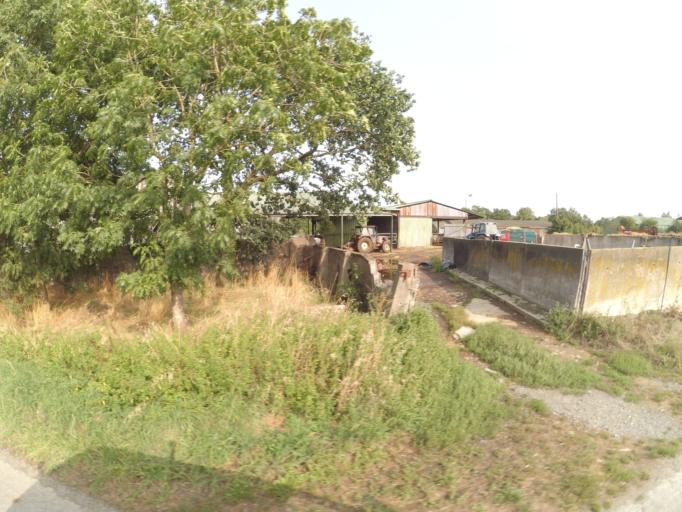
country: FR
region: Pays de la Loire
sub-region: Departement de la Vendee
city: Bouffere
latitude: 46.9382
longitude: -1.3314
